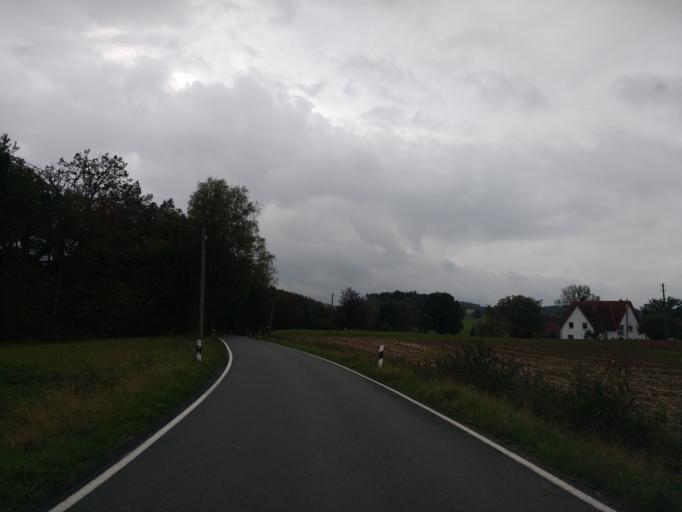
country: DE
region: North Rhine-Westphalia
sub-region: Regierungsbezirk Detmold
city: Lemgo
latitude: 51.9789
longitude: 8.9578
